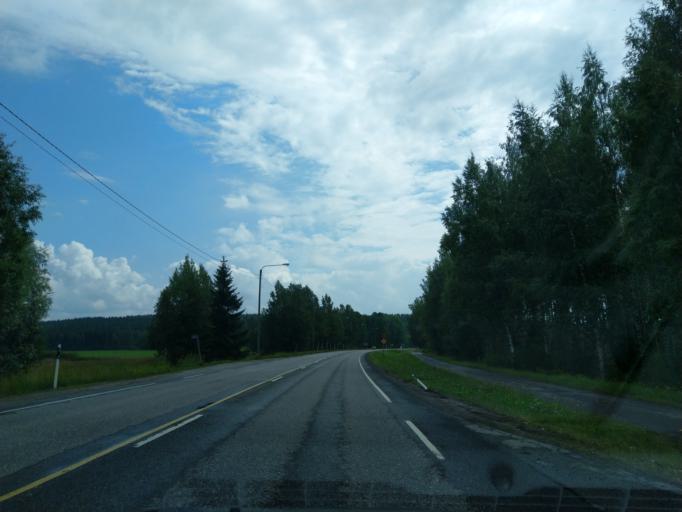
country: FI
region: South Karelia
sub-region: Imatra
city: Parikkala
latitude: 61.5771
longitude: 29.5031
